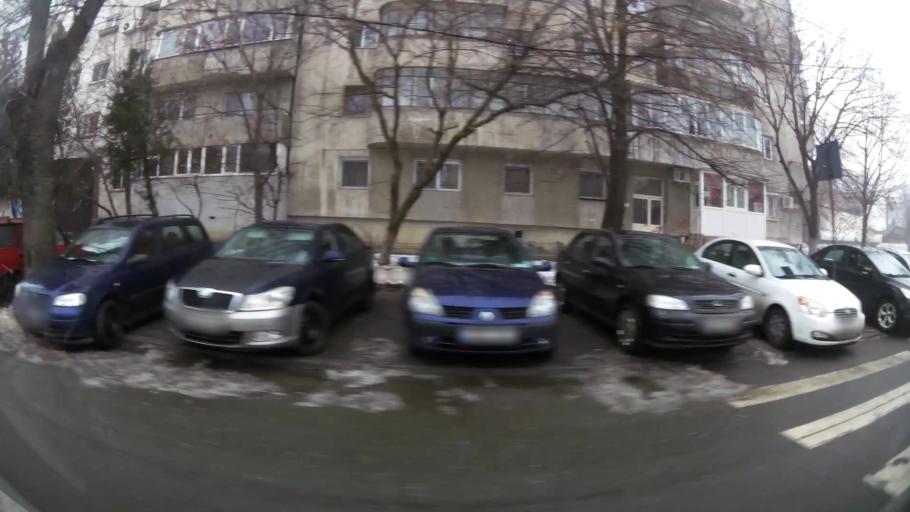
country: RO
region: Ilfov
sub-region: Comuna Chiajna
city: Rosu
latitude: 44.4564
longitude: 26.0554
